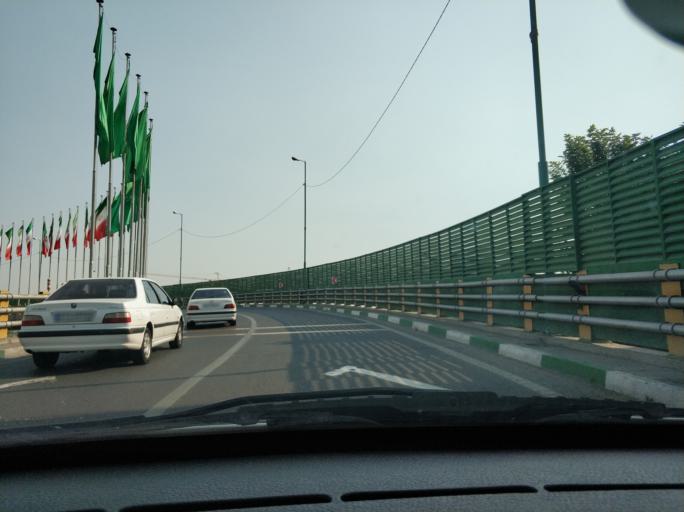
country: IR
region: Tehran
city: Tehran
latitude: 35.7368
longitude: 51.4579
